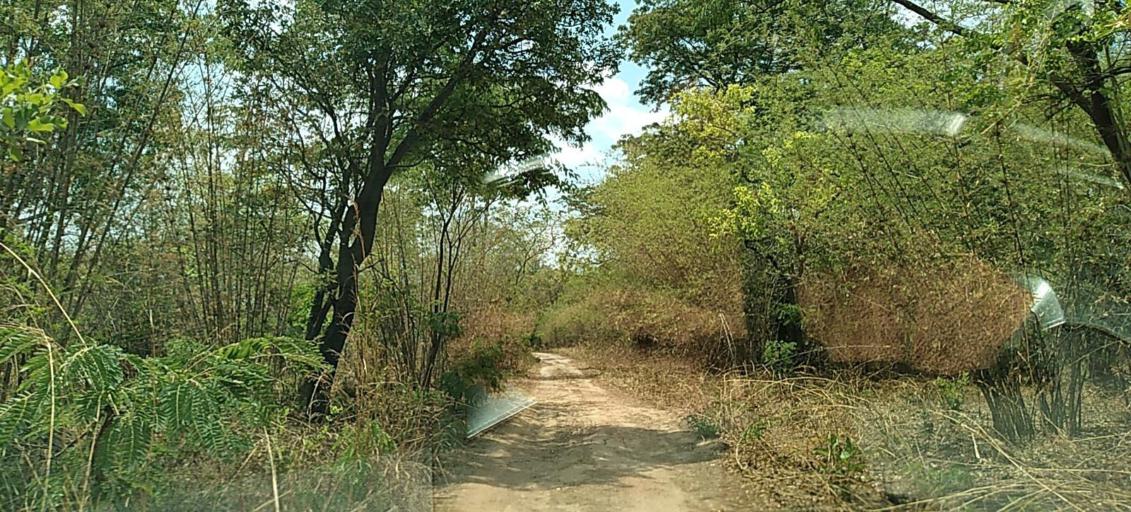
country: ZM
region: Copperbelt
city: Chililabombwe
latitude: -12.4673
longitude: 27.6488
